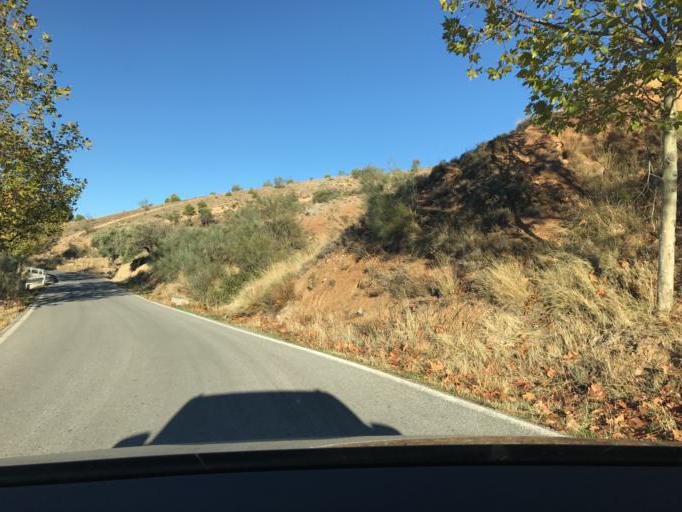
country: ES
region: Andalusia
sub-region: Provincia de Granada
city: Viznar
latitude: 37.2422
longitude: -3.5505
